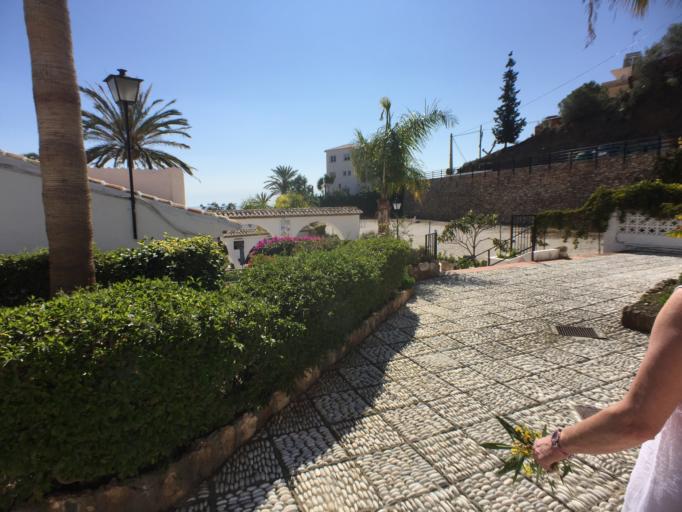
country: ES
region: Andalusia
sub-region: Provincia de Malaga
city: Nerja
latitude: 36.7463
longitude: -3.9059
